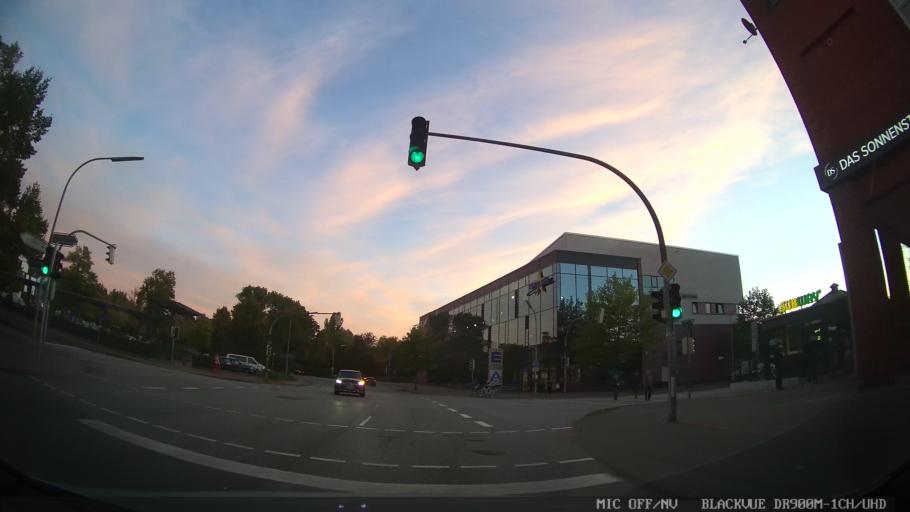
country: DE
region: Schleswig-Holstein
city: Bad Schwartau
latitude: 53.9190
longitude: 10.6949
